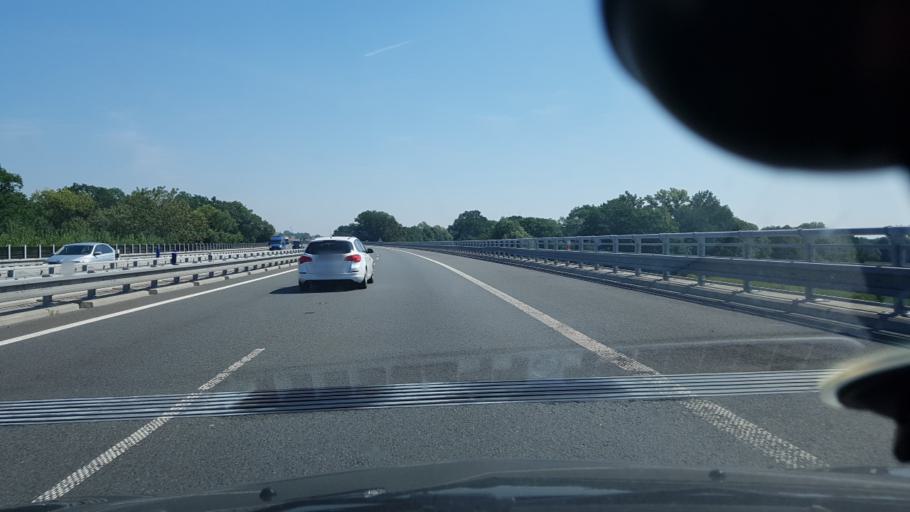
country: CZ
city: Studenka
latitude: 49.7429
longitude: 18.0826
